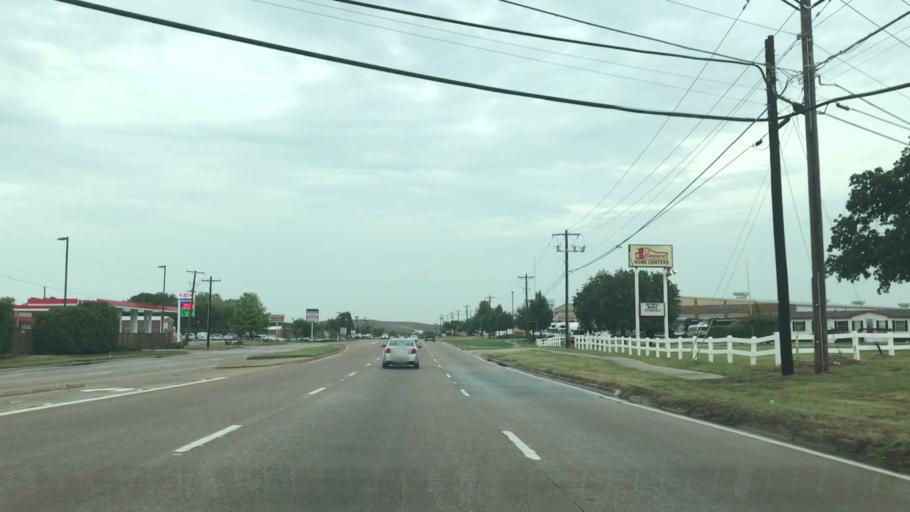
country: US
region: Texas
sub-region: Denton County
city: Lewisville
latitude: 33.0351
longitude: -96.9907
